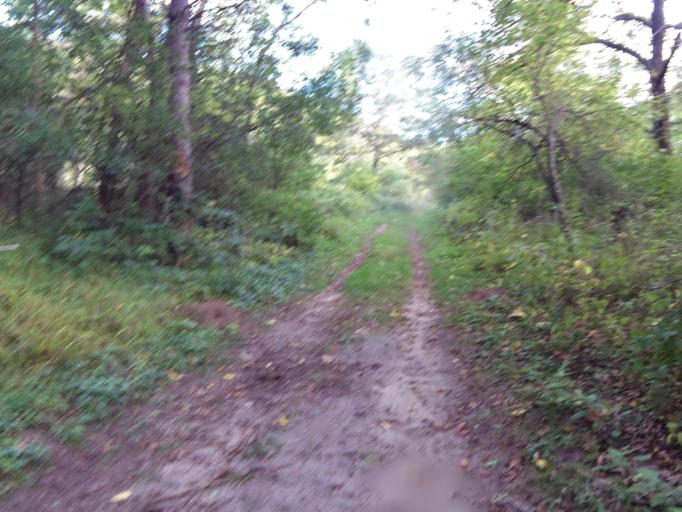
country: US
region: Minnesota
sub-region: Washington County
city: Afton
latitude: 44.8623
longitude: -92.7951
